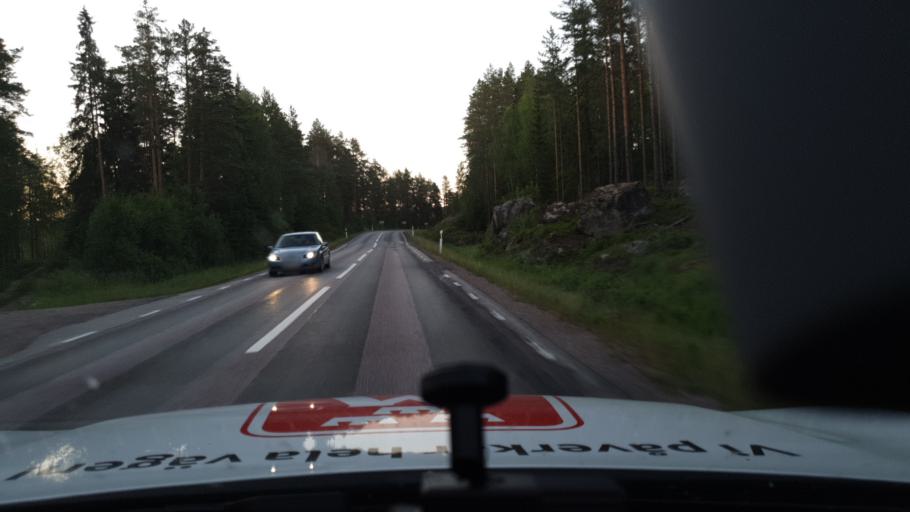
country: SE
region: Vaermland
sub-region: Torsby Kommun
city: Torsby
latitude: 60.3254
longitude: 13.1253
